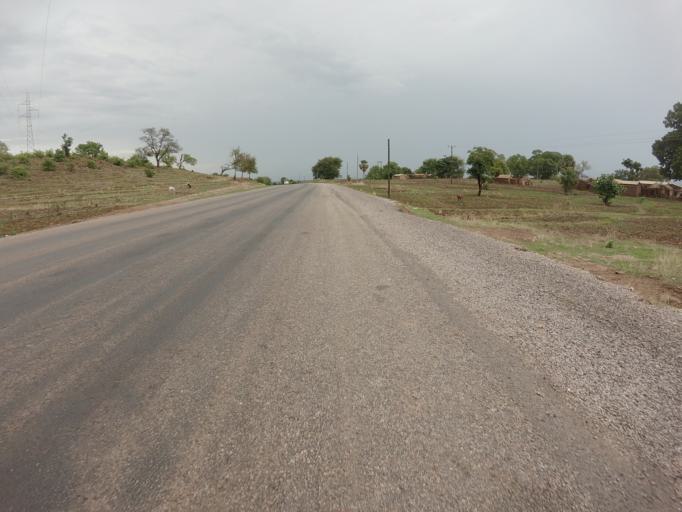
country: GH
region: Upper East
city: Bolgatanga
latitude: 10.8434
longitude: -0.6906
